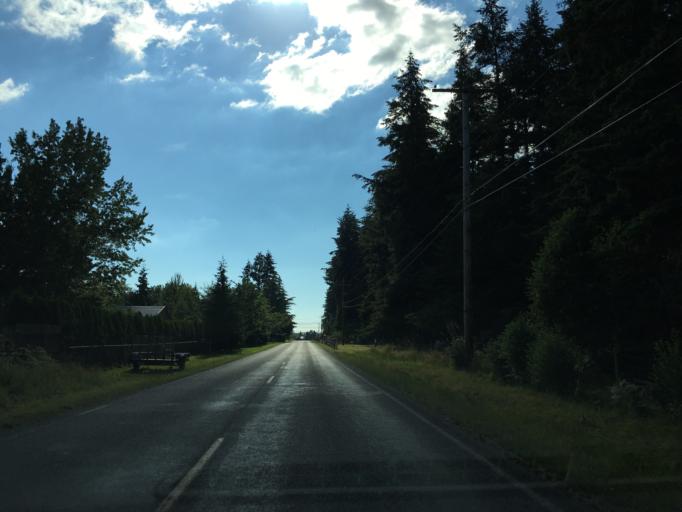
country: US
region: Washington
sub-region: Whatcom County
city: Ferndale
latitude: 48.9207
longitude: -122.5627
